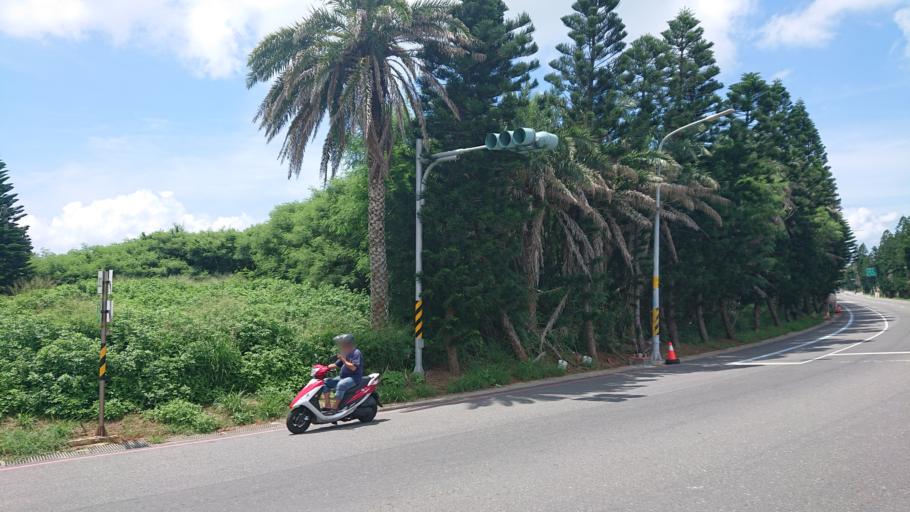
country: TW
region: Taiwan
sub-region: Penghu
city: Ma-kung
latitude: 23.5913
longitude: 119.6130
